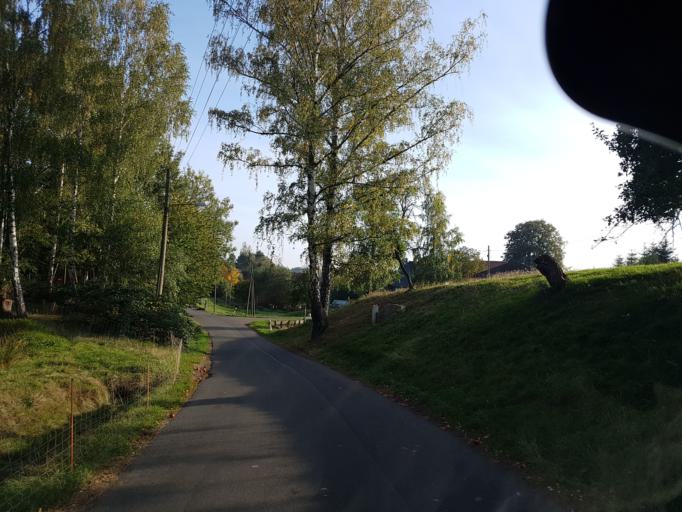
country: DE
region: Saxony
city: Waldheim
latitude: 51.0897
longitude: 13.0007
